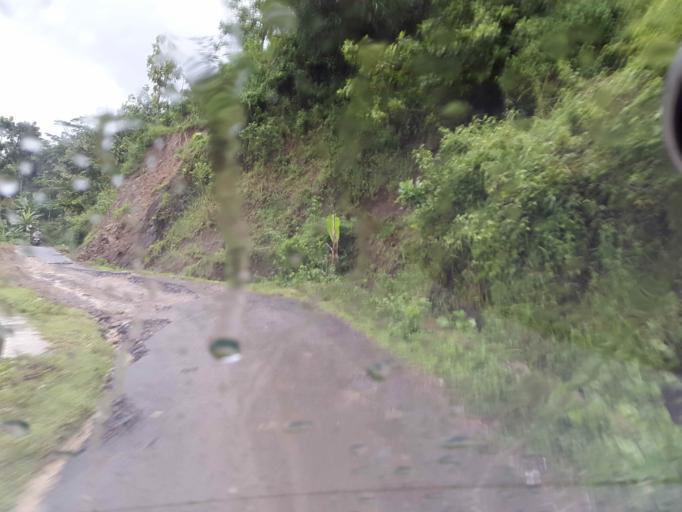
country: ID
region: Central Java
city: Kadumanis
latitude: -7.1708
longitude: 108.9021
